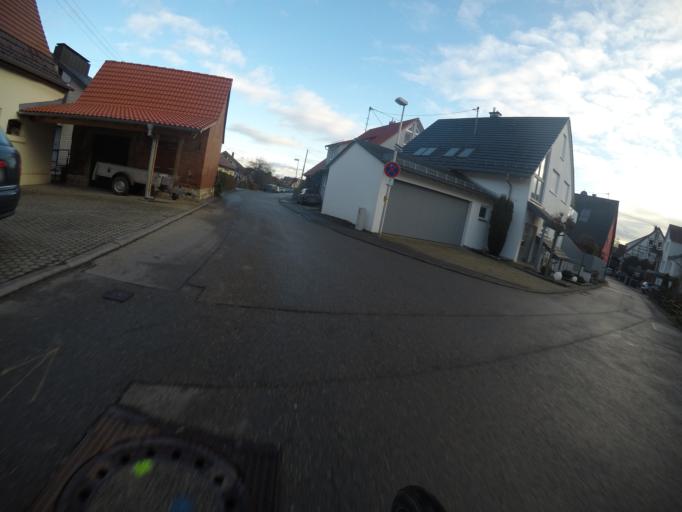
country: DE
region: Baden-Wuerttemberg
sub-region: Tuebingen Region
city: Tuebingen
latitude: 48.5028
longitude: 8.9946
